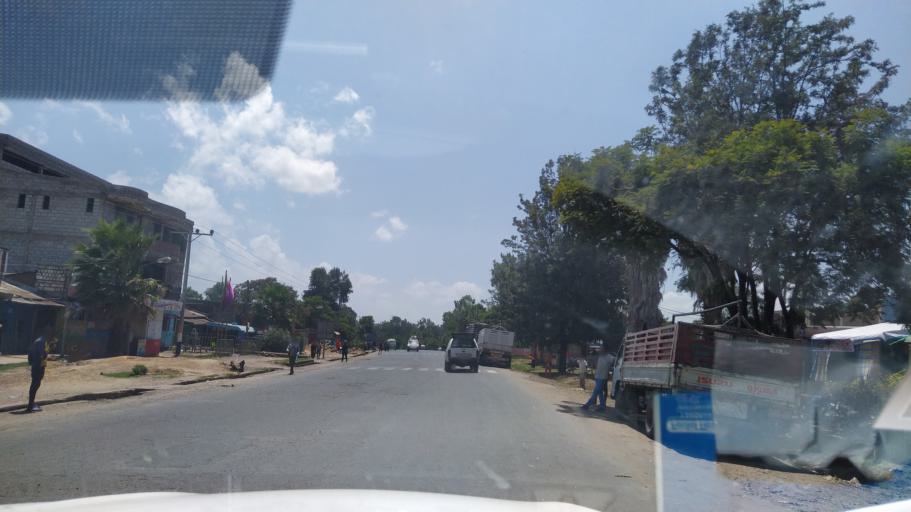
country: ET
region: Southern Nations, Nationalities, and People's Region
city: K'olito
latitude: 7.7391
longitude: 38.1216
